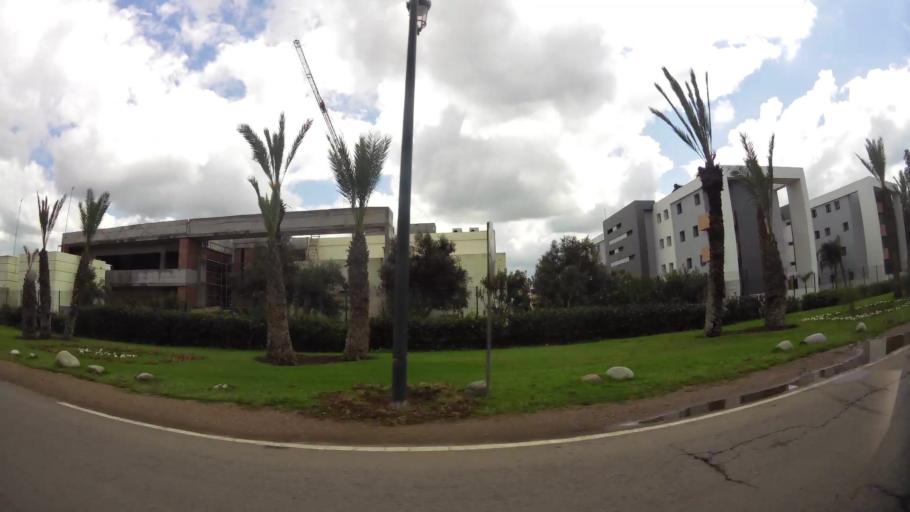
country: MA
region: Chaouia-Ouardigha
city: Nouaseur
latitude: 33.3812
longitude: -7.5700
